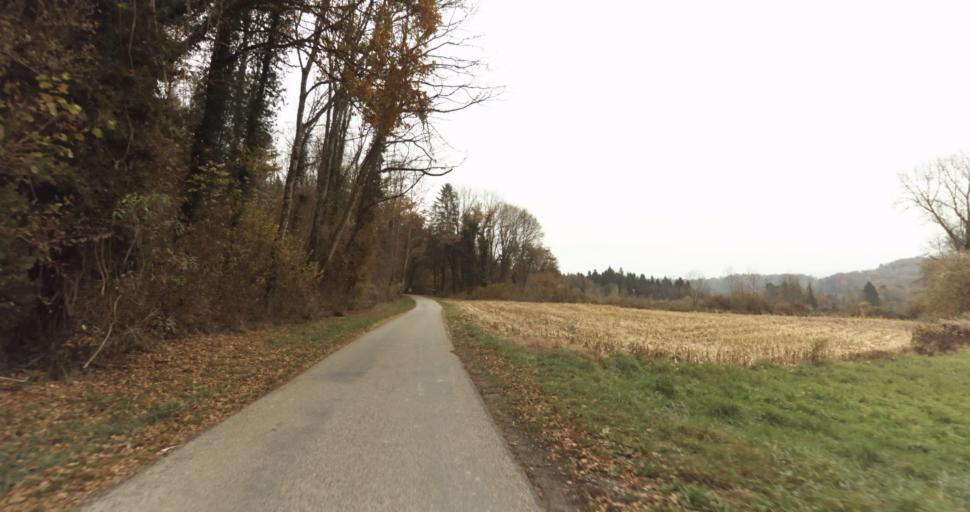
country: FR
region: Rhone-Alpes
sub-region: Departement de la Haute-Savoie
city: Chavanod
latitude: 45.9026
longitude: 6.0514
